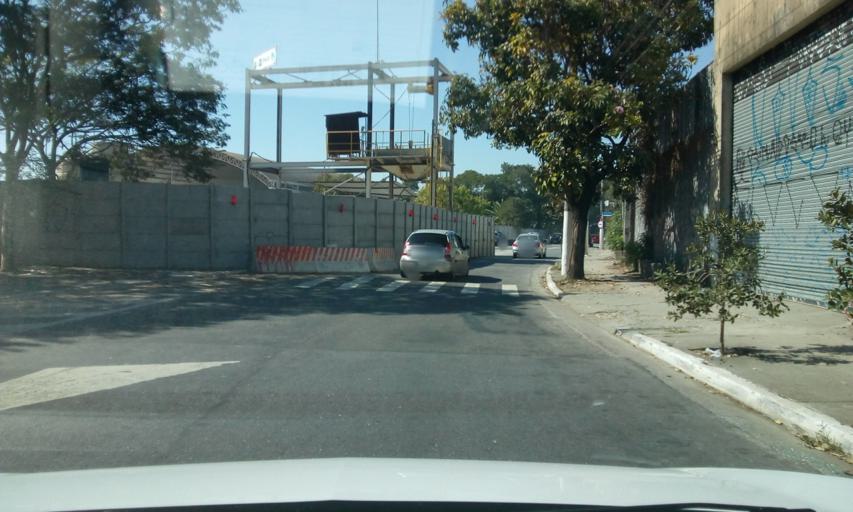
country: BR
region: Sao Paulo
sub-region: Sao Paulo
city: Sao Paulo
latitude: -23.5206
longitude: -46.6447
